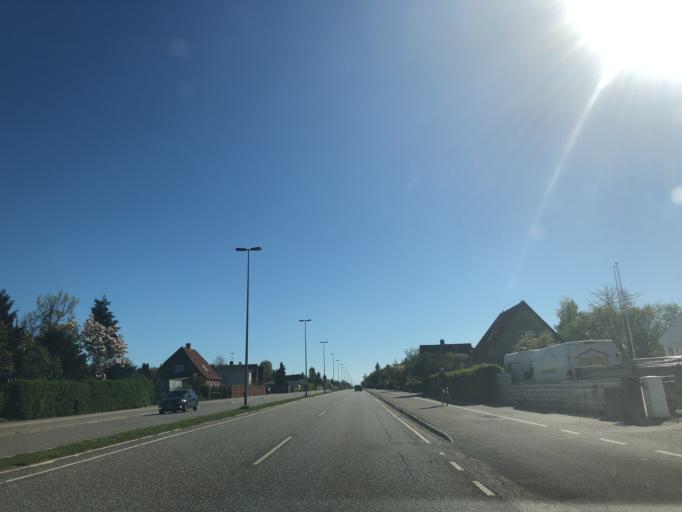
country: DK
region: Zealand
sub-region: Koge Kommune
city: Koge
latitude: 55.4409
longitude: 12.1665
